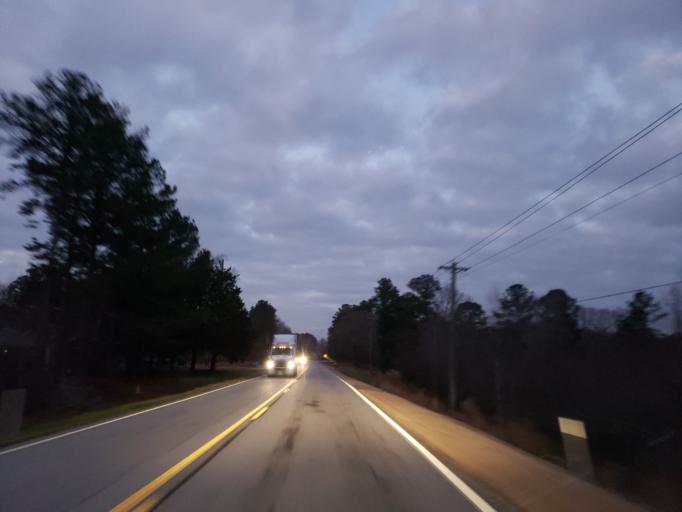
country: US
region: Georgia
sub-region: Carroll County
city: Temple
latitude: 33.8020
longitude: -85.0564
